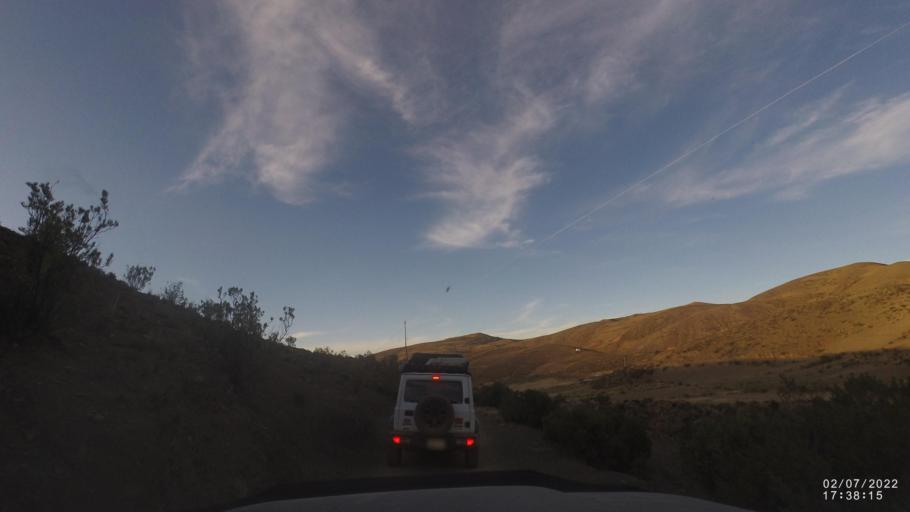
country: BO
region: Cochabamba
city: Irpa Irpa
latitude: -17.8711
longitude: -66.6186
